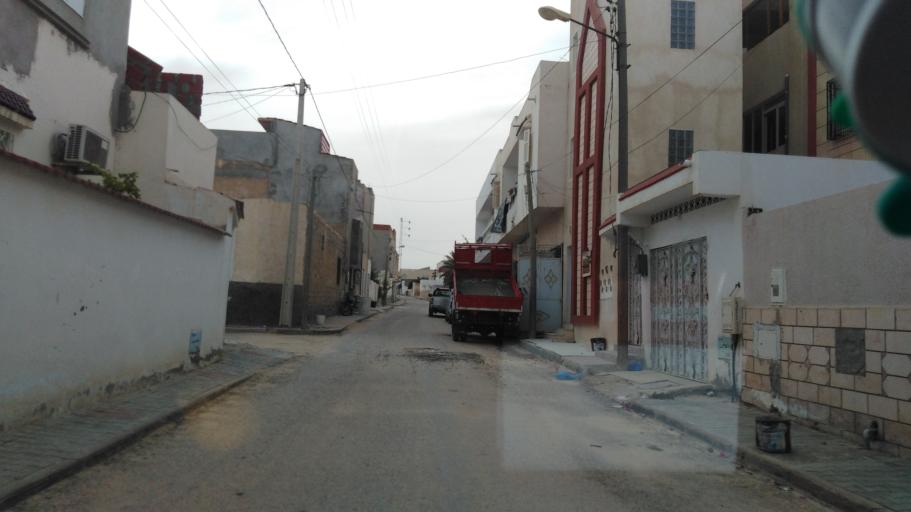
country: TN
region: Qabis
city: Gabes
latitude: 33.9569
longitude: 10.0046
